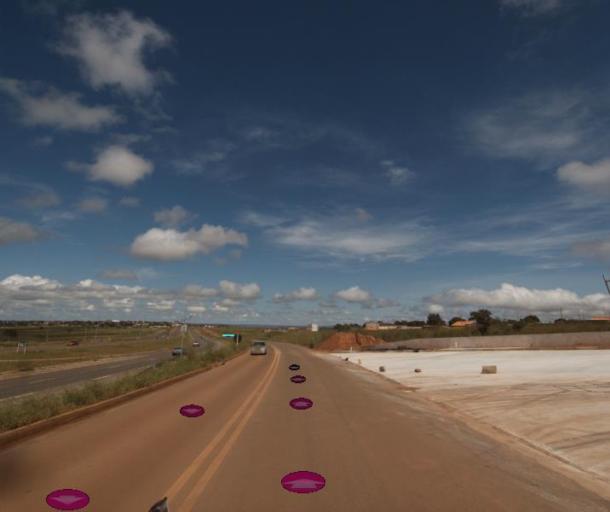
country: BR
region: Federal District
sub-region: Brasilia
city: Brasilia
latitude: -15.7415
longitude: -48.3145
